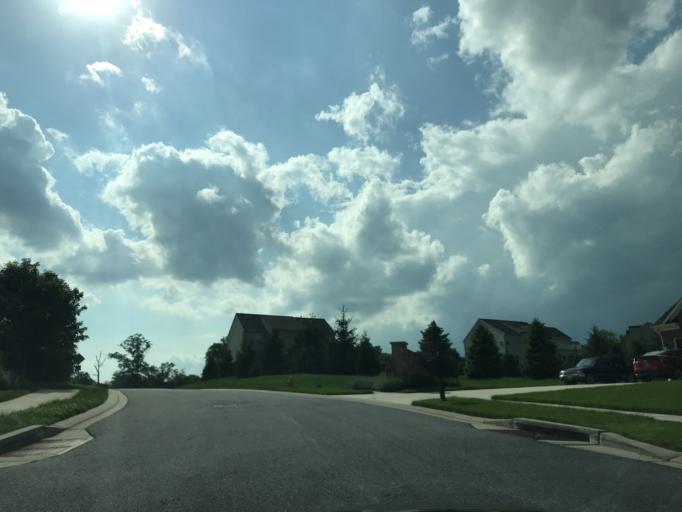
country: US
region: Maryland
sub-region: Harford County
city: Bel Air North
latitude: 39.5544
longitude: -76.3884
